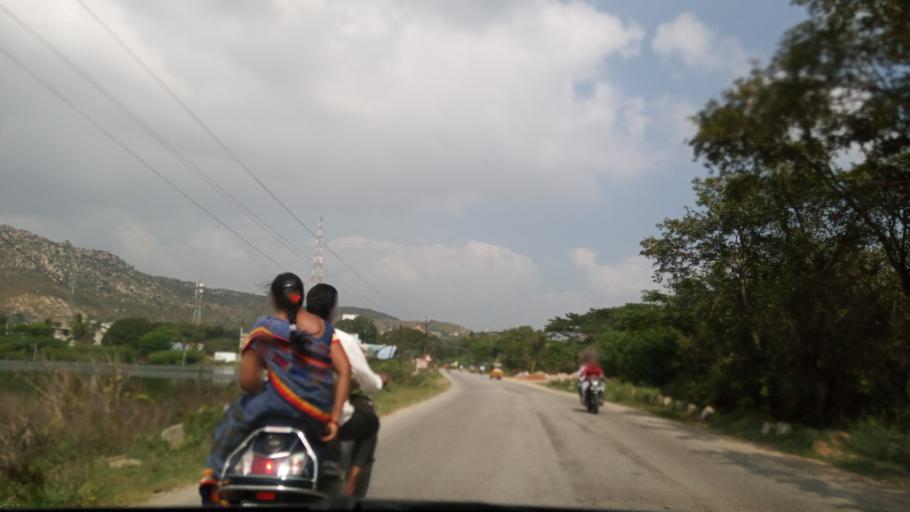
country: IN
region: Andhra Pradesh
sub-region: Chittoor
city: Madanapalle
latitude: 13.5765
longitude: 78.5194
